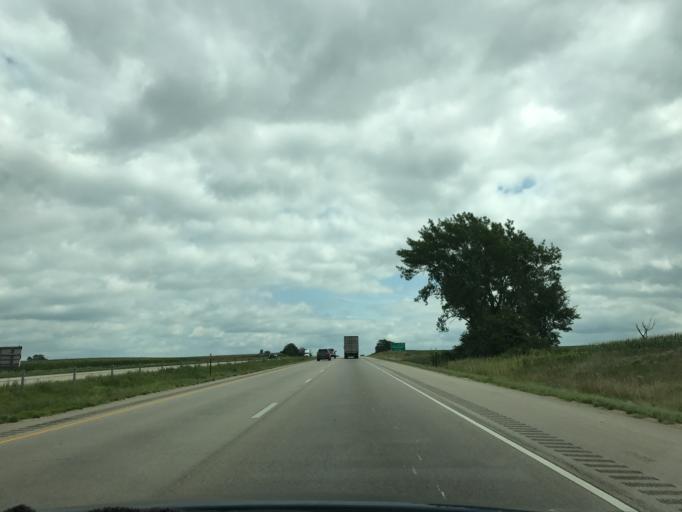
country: US
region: Illinois
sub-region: LaSalle County
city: Marseilles
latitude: 41.3754
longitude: -88.7218
